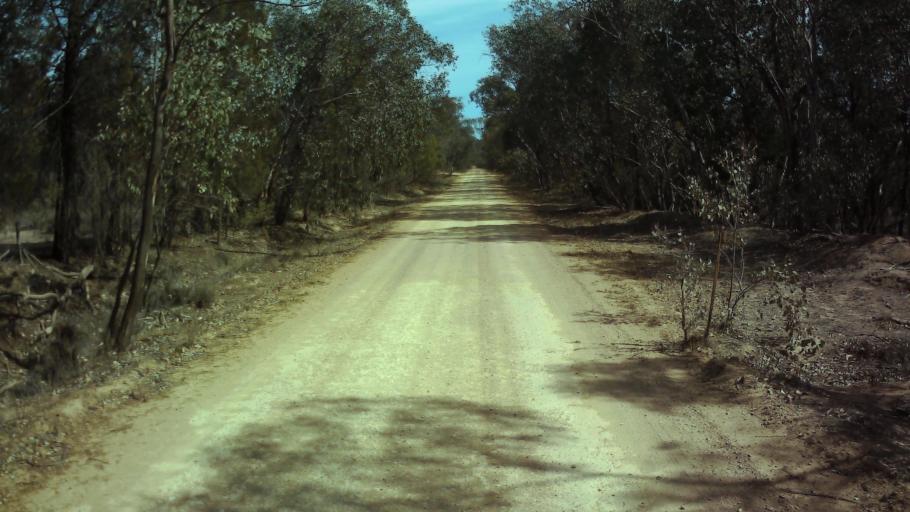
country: AU
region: New South Wales
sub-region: Weddin
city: Grenfell
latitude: -33.8775
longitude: 148.1497
